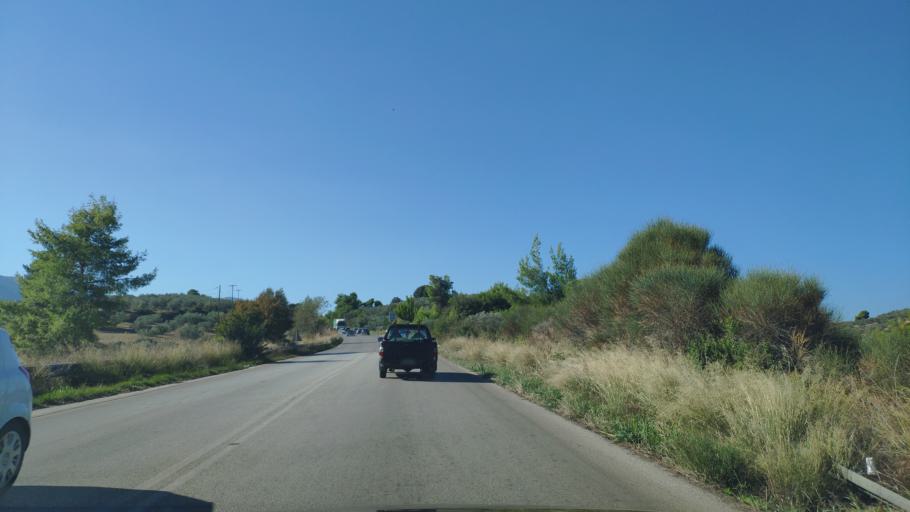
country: GR
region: Peloponnese
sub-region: Nomos Korinthias
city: Khiliomodhi
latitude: 37.8227
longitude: 22.8804
